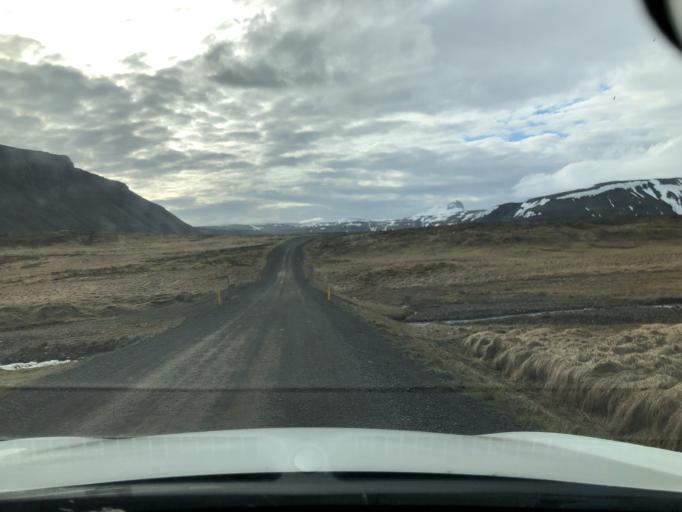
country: IS
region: West
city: Stykkisholmur
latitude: 64.9763
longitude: -22.6018
